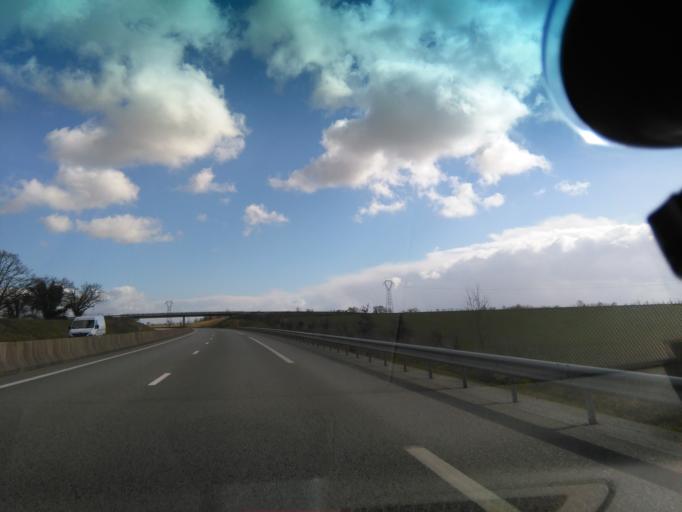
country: FR
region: Lower Normandy
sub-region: Departement de l'Orne
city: Mortree
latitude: 48.6647
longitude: 0.0649
